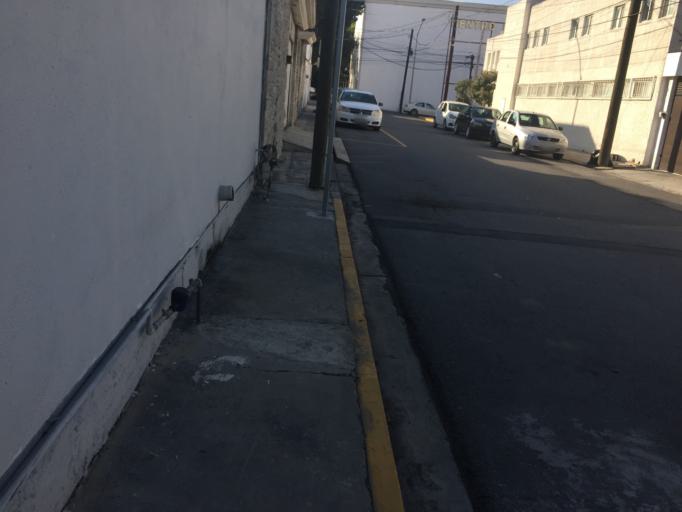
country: MX
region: Nuevo Leon
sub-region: San Pedro Garza Garcia
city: San Pedro Garza Garcia
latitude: 25.6572
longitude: -100.3961
